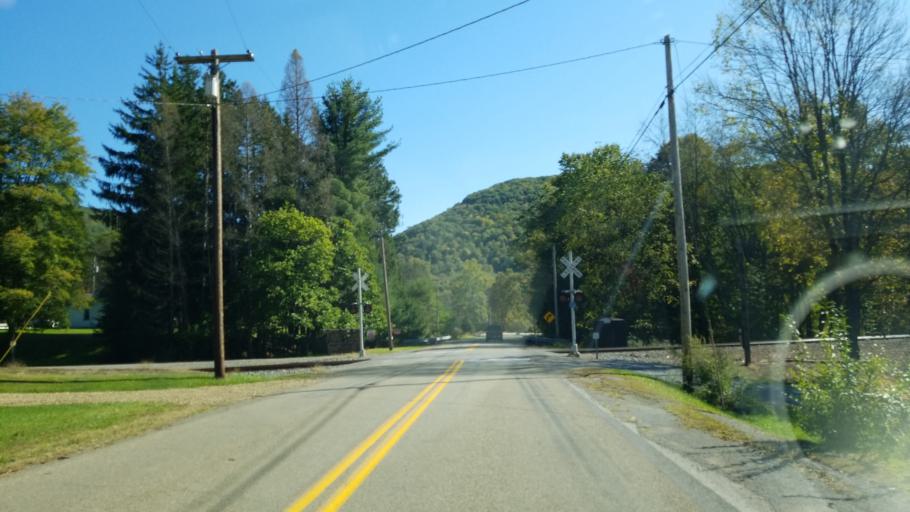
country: US
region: Pennsylvania
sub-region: Elk County
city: Saint Marys
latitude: 41.2868
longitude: -78.3946
